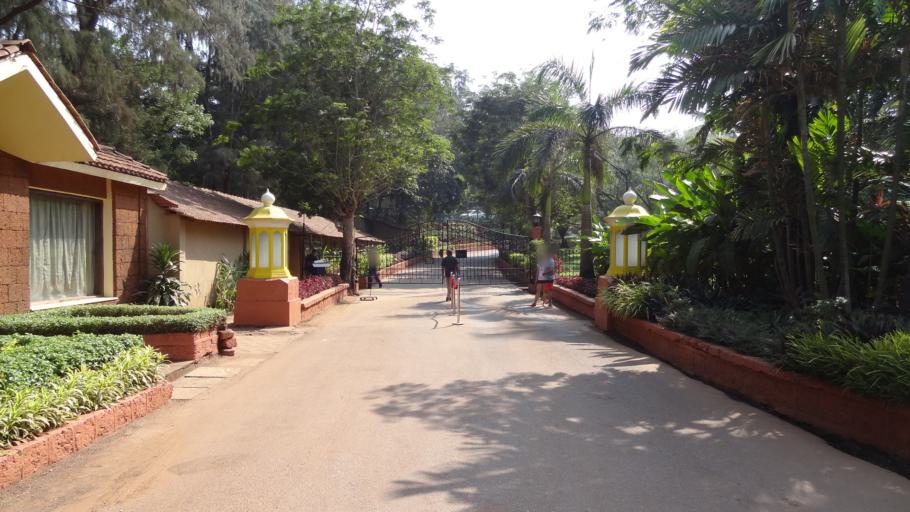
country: IN
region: Goa
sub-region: North Goa
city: Candolim
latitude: 15.4984
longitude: 73.7683
